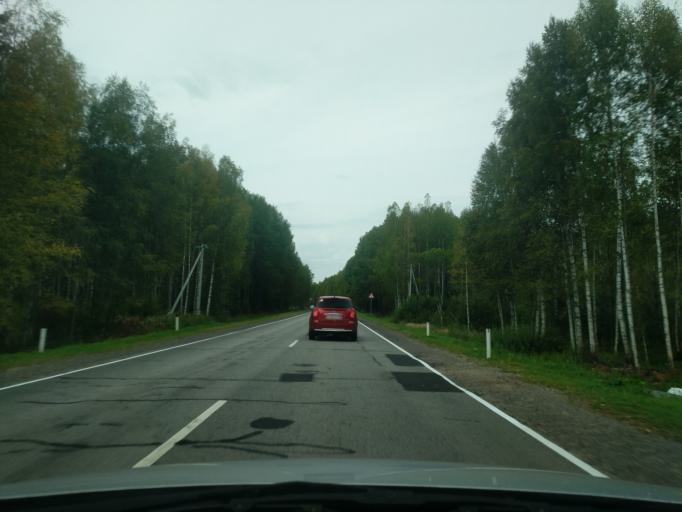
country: RU
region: Kirov
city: Kotel'nich
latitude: 58.2713
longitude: 48.0795
